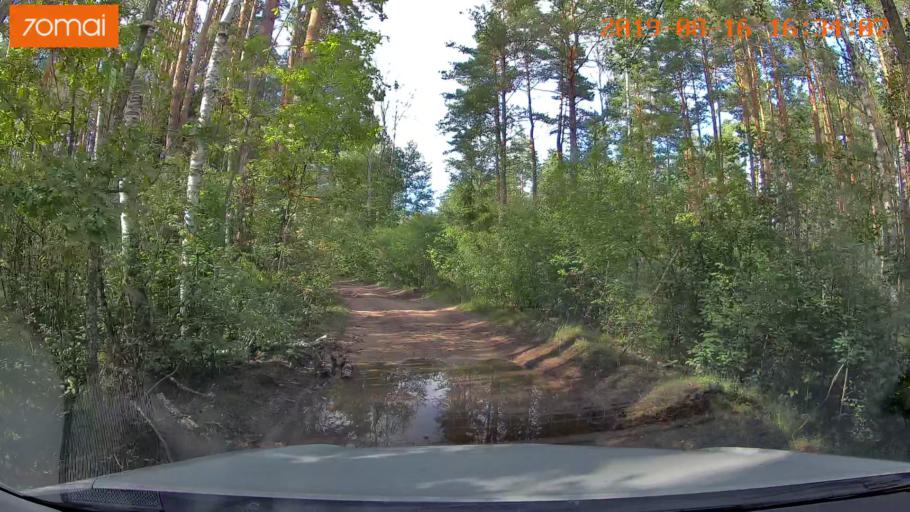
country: BY
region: Mogilev
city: Asipovichy
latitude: 53.2288
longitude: 28.7755
